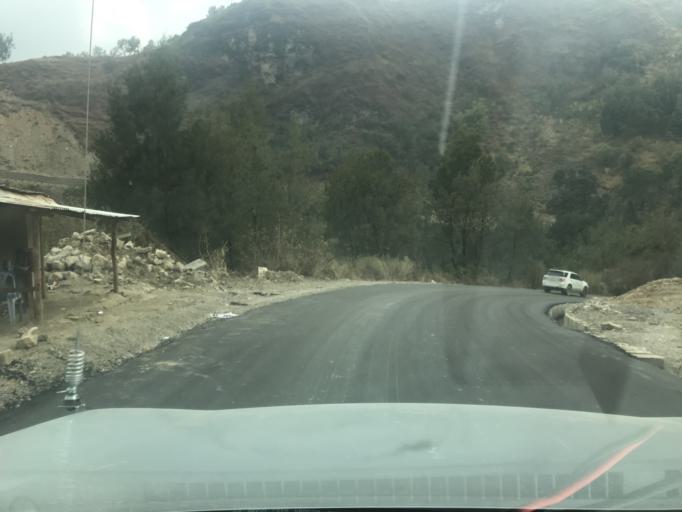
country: TL
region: Manufahi
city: Same
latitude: -8.8979
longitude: 125.5916
